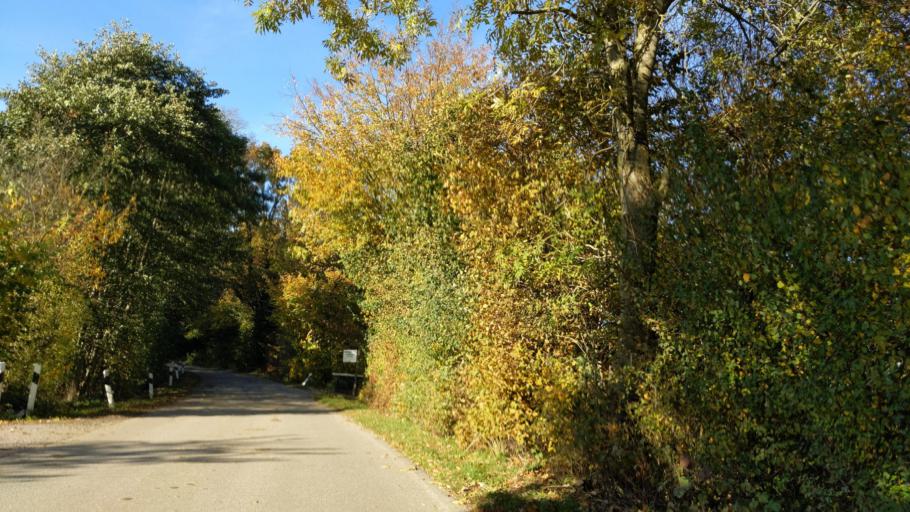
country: DE
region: Schleswig-Holstein
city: Kasseedorf
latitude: 54.1349
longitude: 10.7281
